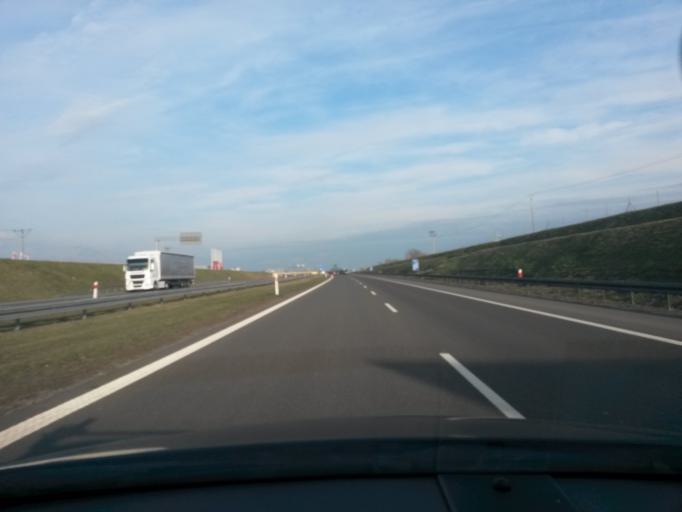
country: PL
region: Lodz Voivodeship
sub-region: Powiat zgierski
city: Strykow
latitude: 51.8897
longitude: 19.5744
